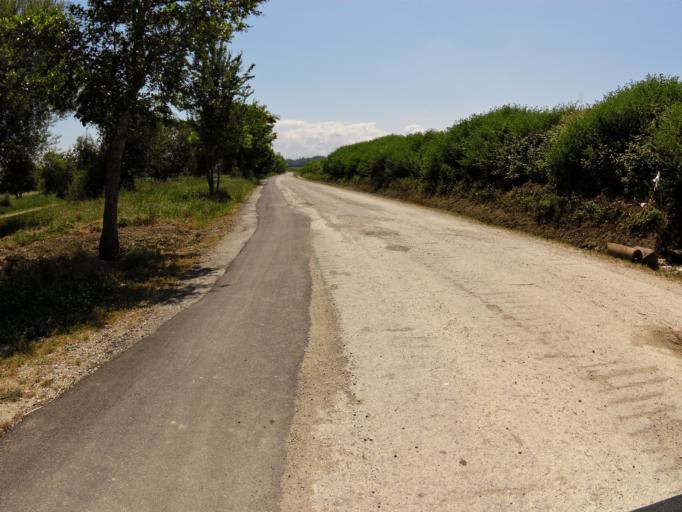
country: PT
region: Coimbra
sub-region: Montemor-O-Velho
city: Montemor-o-Velho
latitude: 40.1480
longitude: -8.7153
